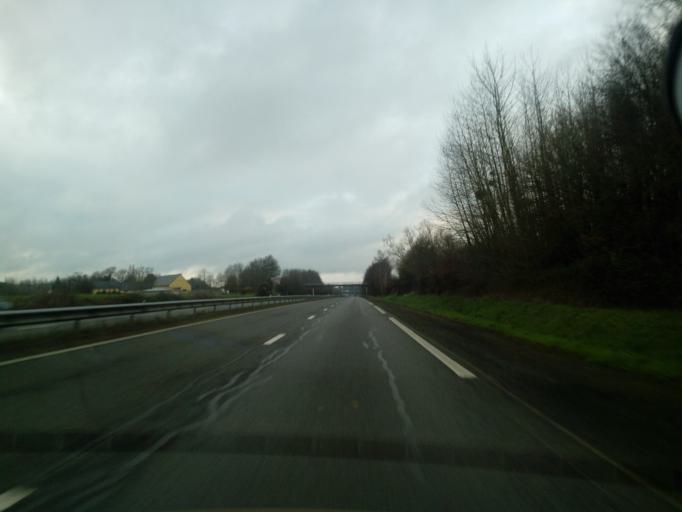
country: FR
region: Brittany
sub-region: Departement d'Ille-et-Vilaine
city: Saint-Meen-le-Grand
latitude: 48.1811
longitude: -2.2048
